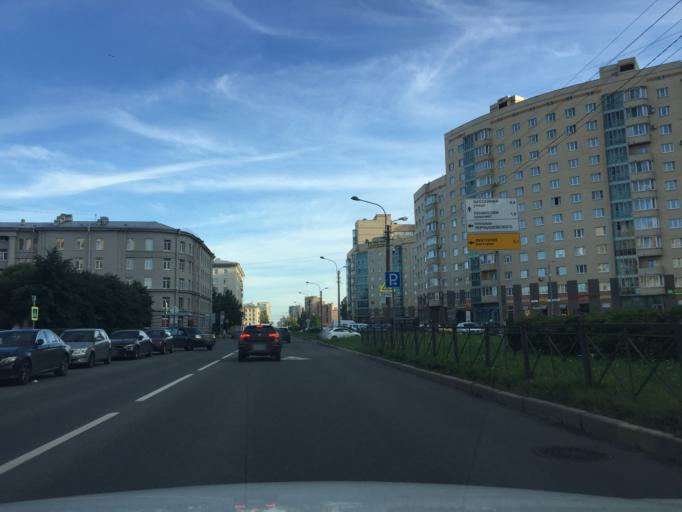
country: RU
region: St.-Petersburg
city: Kupchino
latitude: 59.8686
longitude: 30.3138
